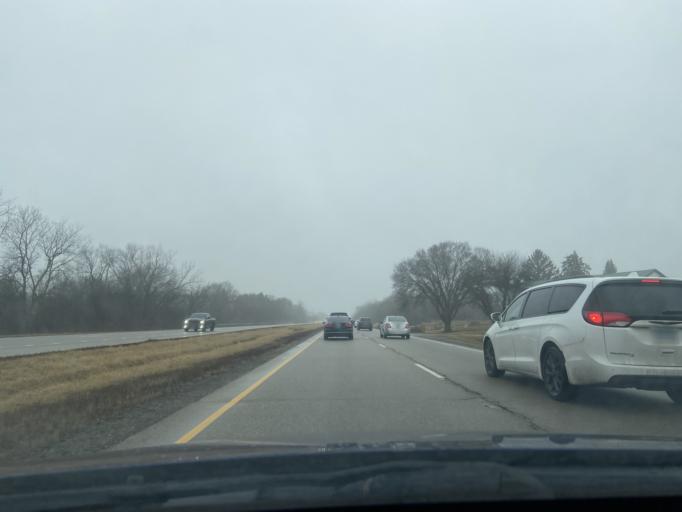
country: US
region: Illinois
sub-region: Lake County
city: Wauconda
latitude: 42.2464
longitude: -88.1281
